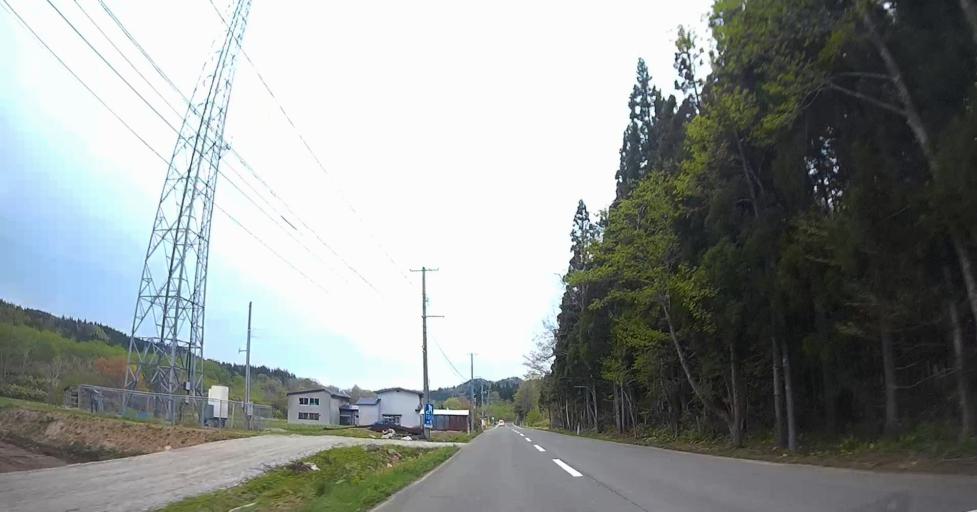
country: JP
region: Aomori
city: Goshogawara
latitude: 41.1309
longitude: 140.5196
